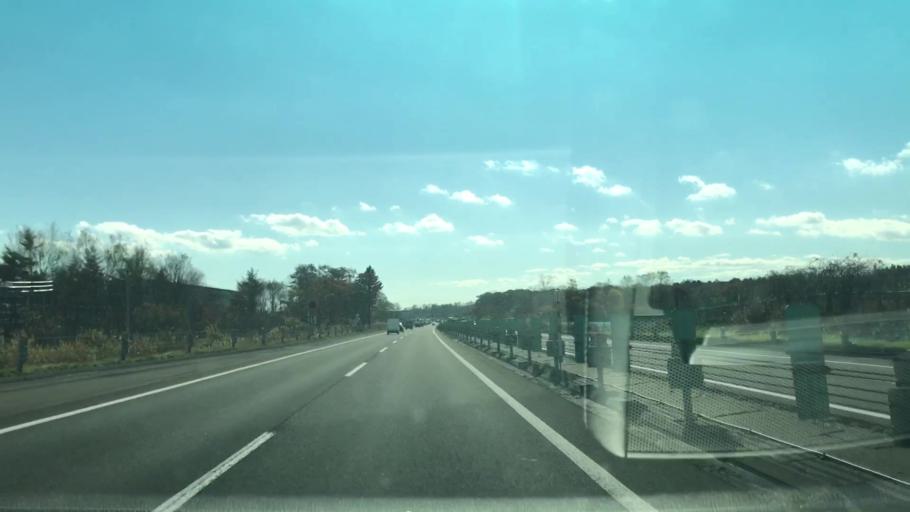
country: JP
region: Hokkaido
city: Kitahiroshima
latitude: 42.9000
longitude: 141.5505
